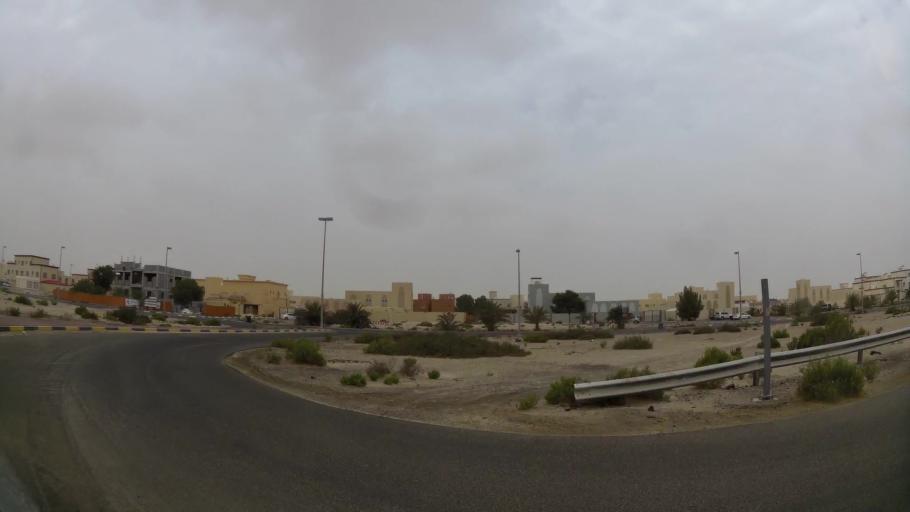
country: AE
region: Abu Dhabi
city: Abu Dhabi
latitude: 24.3936
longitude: 54.7441
